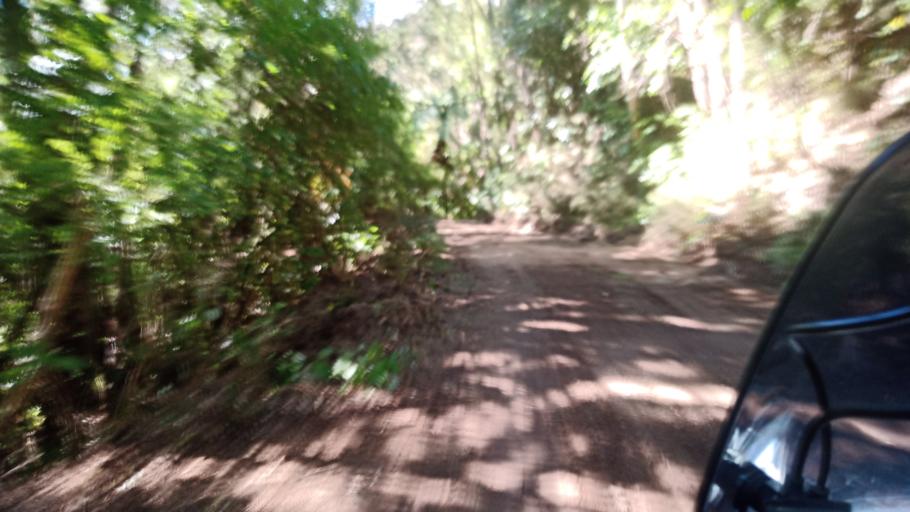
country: NZ
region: Hawke's Bay
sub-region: Wairoa District
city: Wairoa
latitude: -39.0008
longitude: 177.0604
